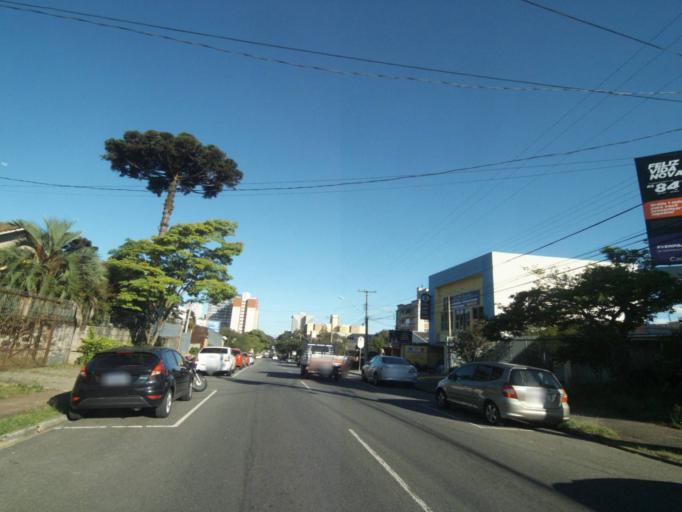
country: BR
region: Parana
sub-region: Curitiba
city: Curitiba
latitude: -25.3980
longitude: -49.2500
